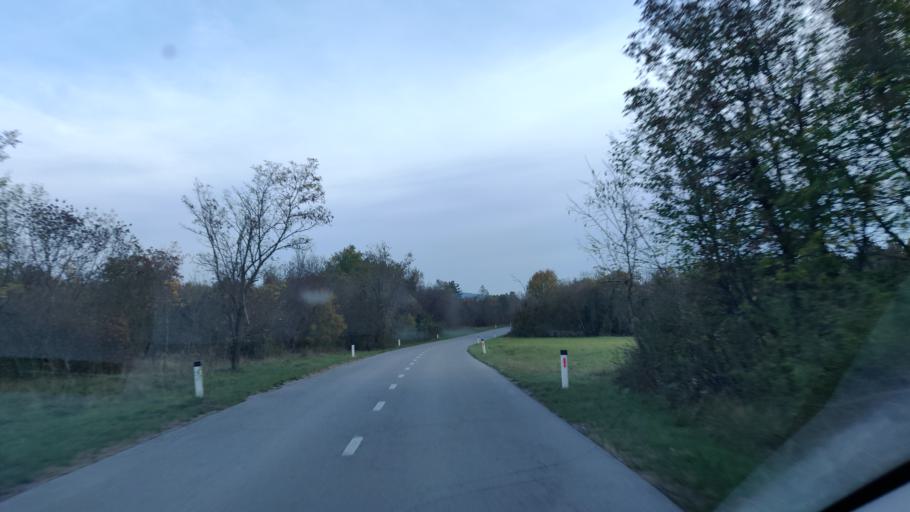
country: SI
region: Sezana
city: Sezana
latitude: 45.7578
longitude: 13.9158
